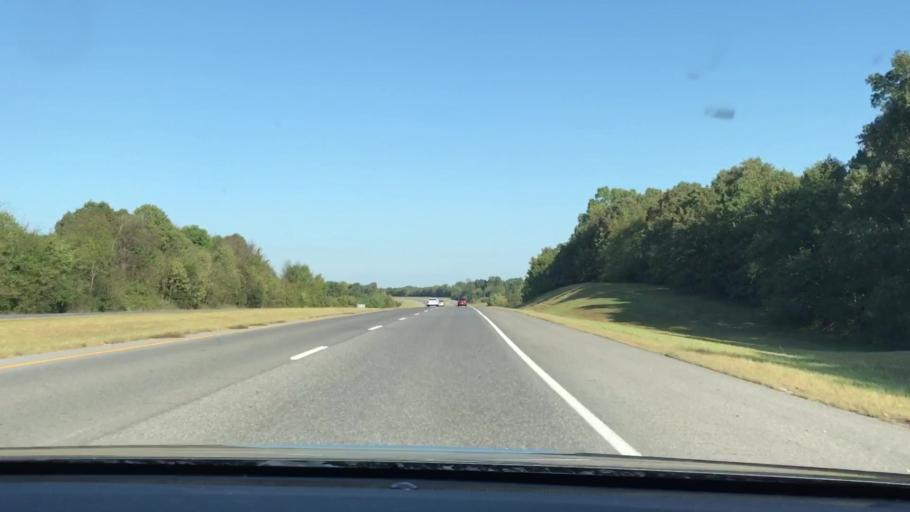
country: US
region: Kentucky
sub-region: Marshall County
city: Benton
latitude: 36.7799
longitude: -88.3225
